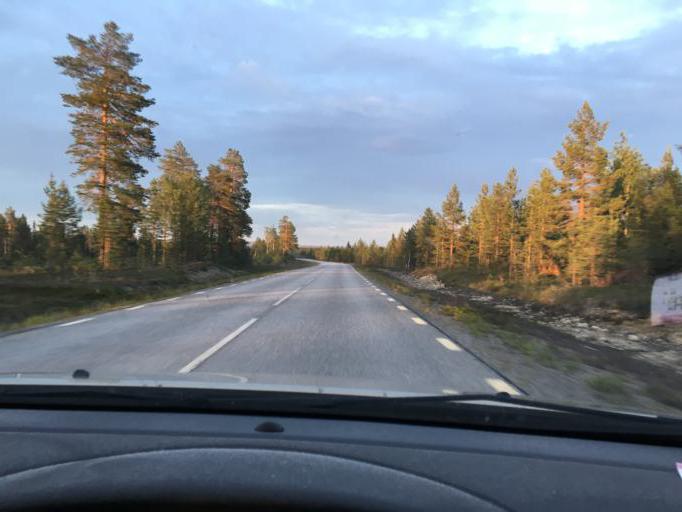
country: SE
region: Norrbotten
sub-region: Kalix Kommun
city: Toere
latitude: 66.0551
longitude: 22.4577
